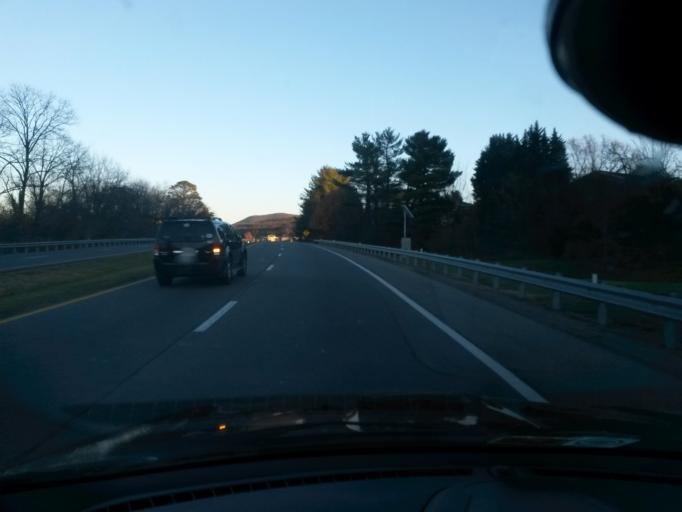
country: US
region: Virginia
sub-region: Roanoke County
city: Cave Spring
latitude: 37.2248
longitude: -79.9953
